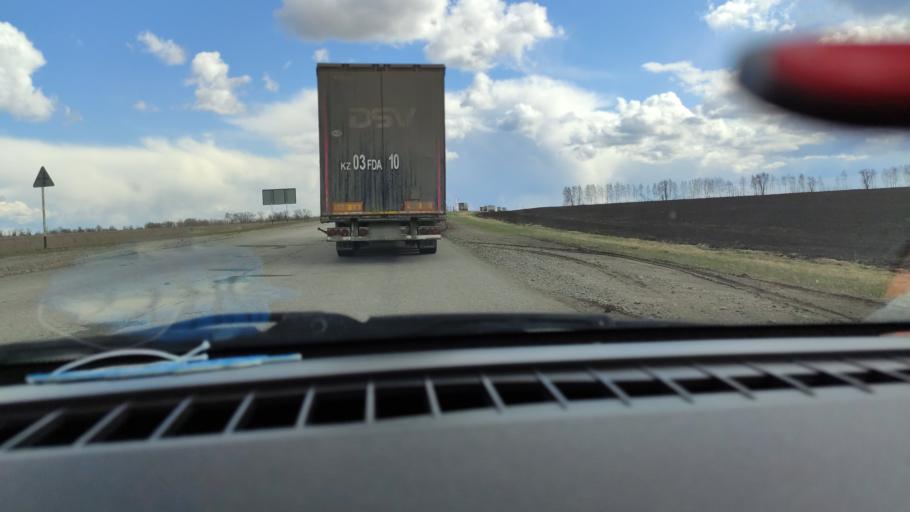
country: RU
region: Samara
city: Varlamovo
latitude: 53.1119
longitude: 48.3527
